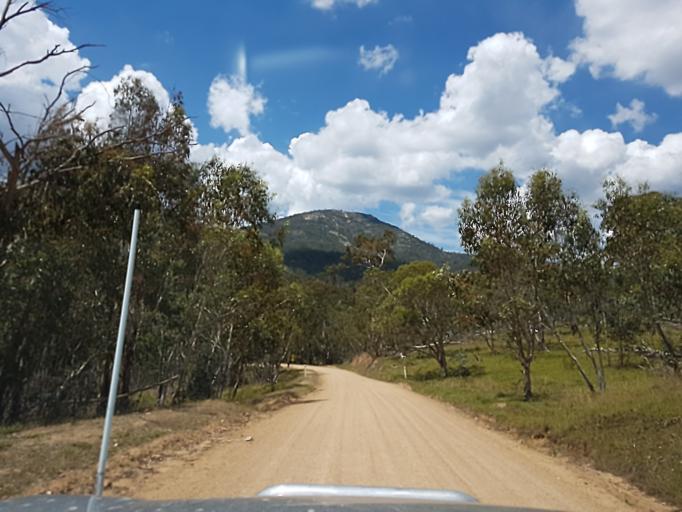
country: AU
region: Victoria
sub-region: Alpine
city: Mount Beauty
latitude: -36.8969
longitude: 147.8852
